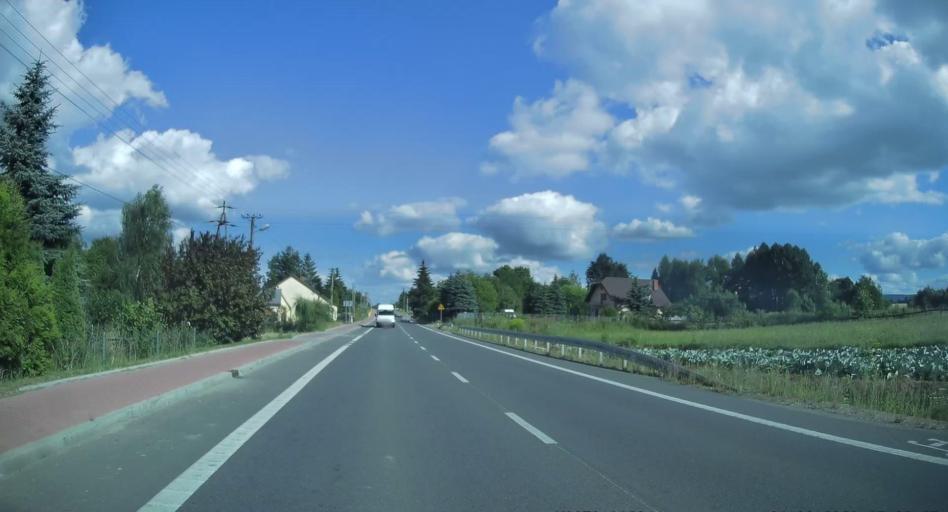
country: PL
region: Swietokrzyskie
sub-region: Powiat kielecki
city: Bodzentyn
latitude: 50.9354
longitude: 20.9616
